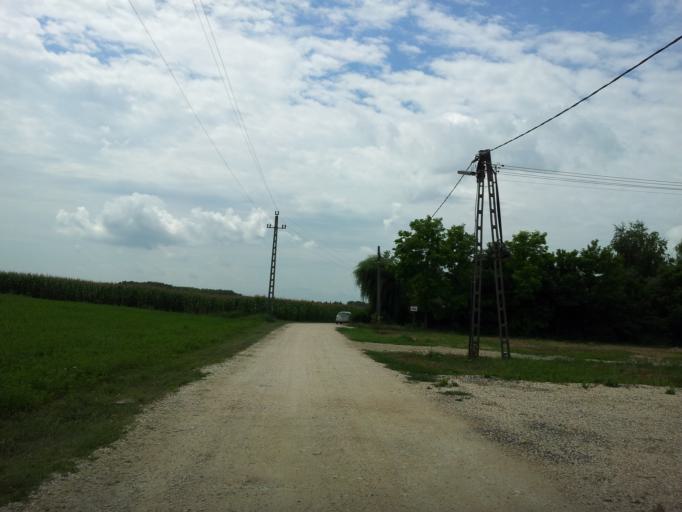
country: HU
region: Pest
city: Szigetcsep
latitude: 47.2369
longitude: 18.9776
